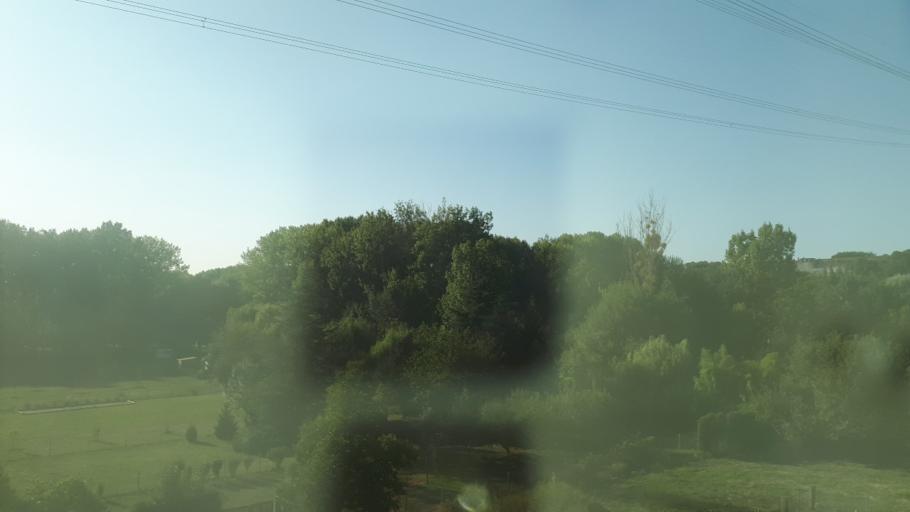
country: FR
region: Centre
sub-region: Departement d'Indre-et-Loire
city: Vouvray
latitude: 47.4069
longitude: 0.8139
